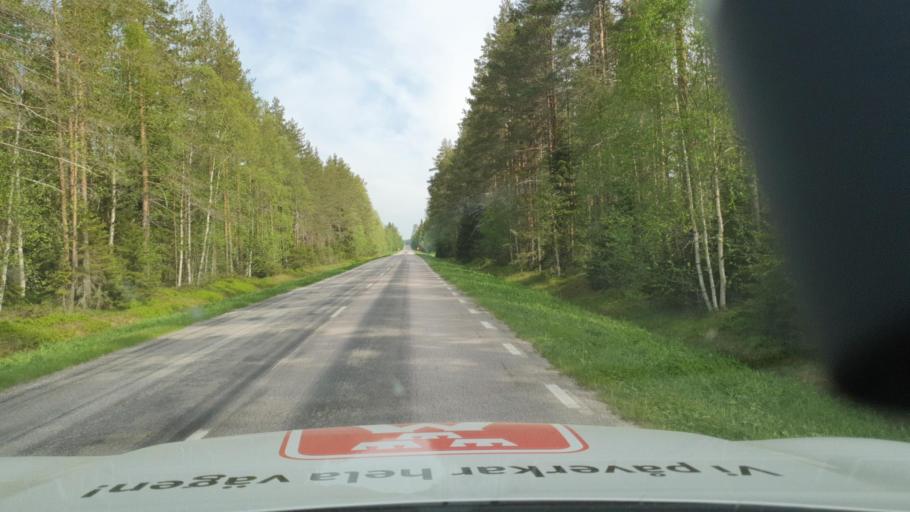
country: SE
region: Vaesterbotten
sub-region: Umea Kommun
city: Hoernefors
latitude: 63.6891
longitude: 19.9200
